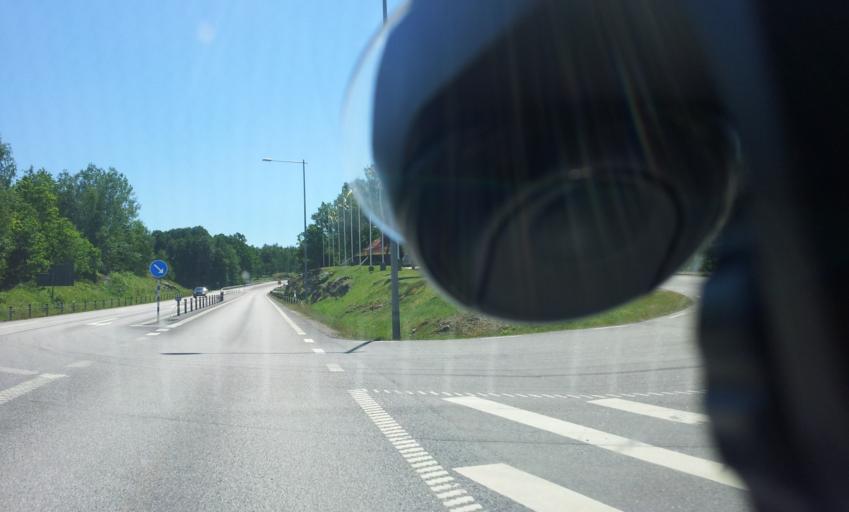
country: SE
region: Kalmar
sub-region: Vasterviks Kommun
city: Forserum
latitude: 57.9801
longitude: 16.4833
